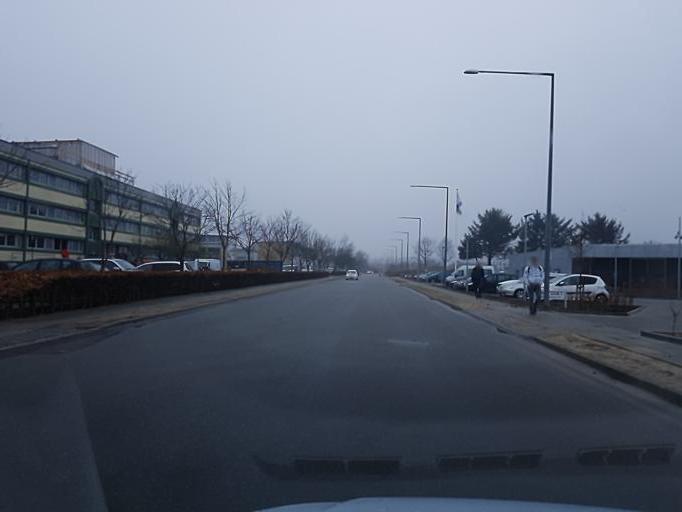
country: DK
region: South Denmark
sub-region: Esbjerg Kommune
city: Esbjerg
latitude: 55.4848
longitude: 8.4911
